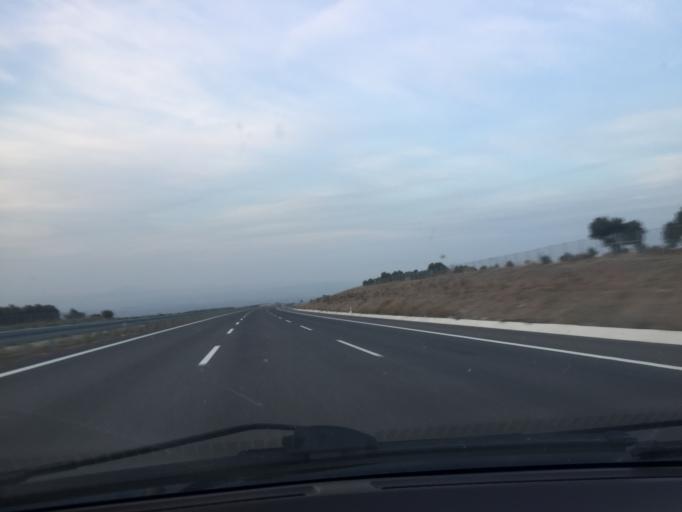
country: TR
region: Manisa
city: Halitpasa
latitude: 38.6805
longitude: 27.6425
